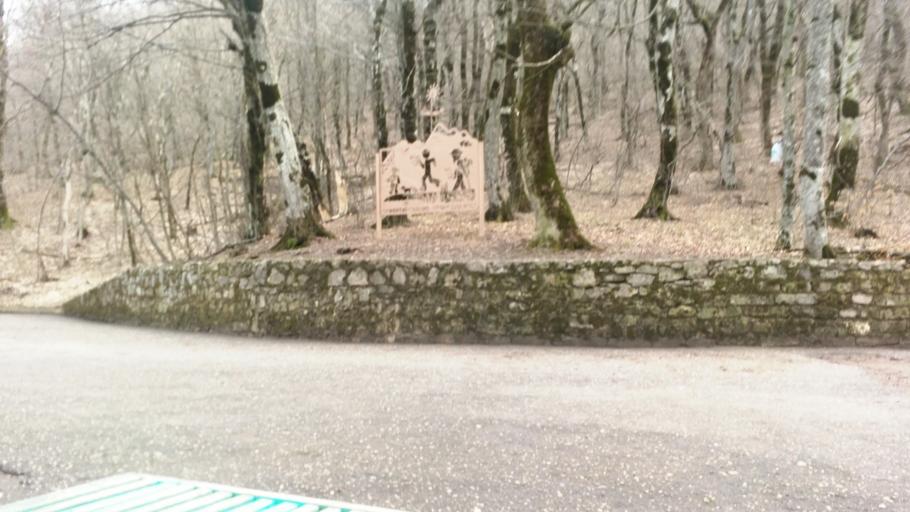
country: RU
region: Stavropol'skiy
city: Zheleznovodsk
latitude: 44.1427
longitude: 43.0282
